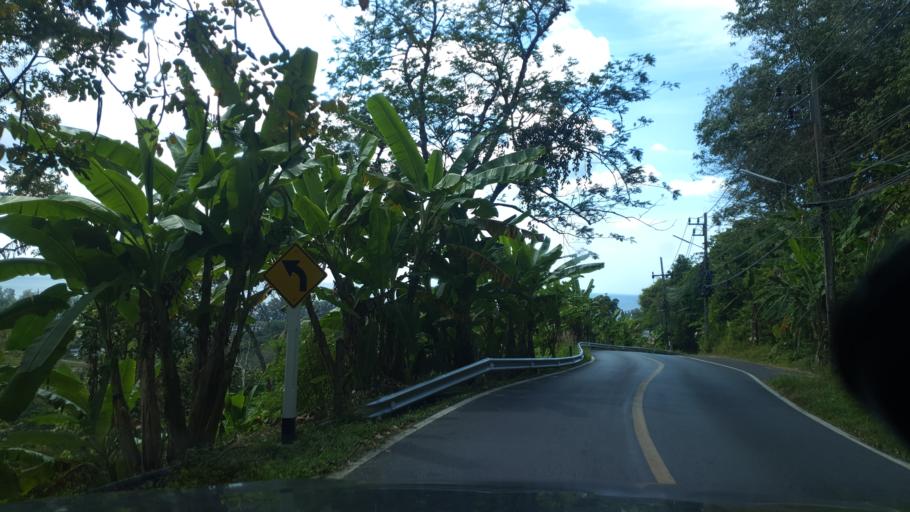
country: TH
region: Phuket
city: Thalang
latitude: 8.0638
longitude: 98.2859
